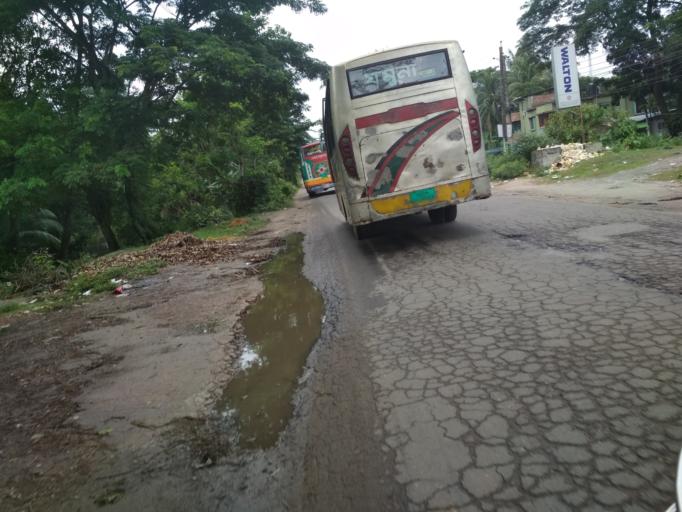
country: BD
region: Chittagong
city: Lakshmipur
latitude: 22.9456
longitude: 90.8214
